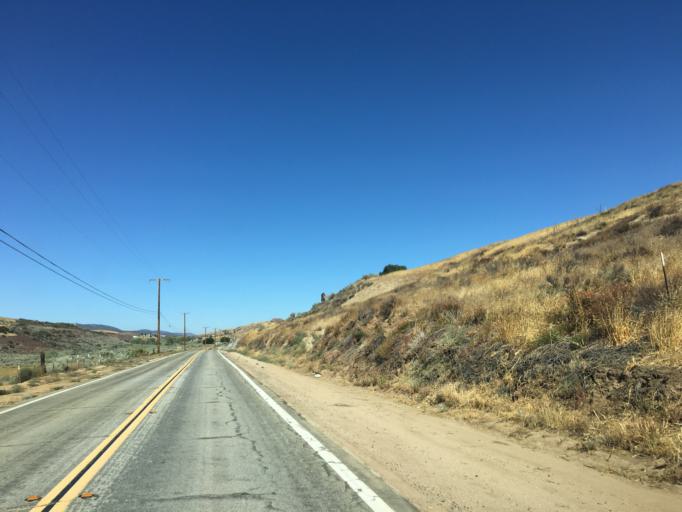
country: US
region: California
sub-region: Los Angeles County
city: Leona Valley
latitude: 34.6213
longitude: -118.2977
